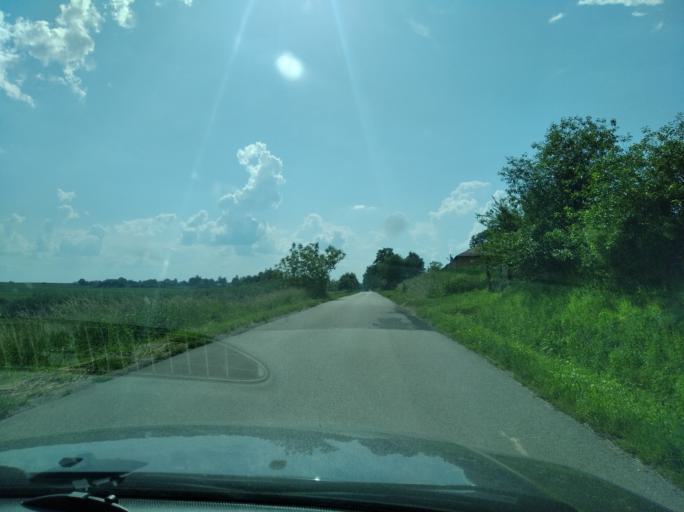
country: PL
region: Subcarpathian Voivodeship
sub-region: Powiat jaroslawski
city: Rokietnica
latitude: 49.9258
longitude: 22.7173
